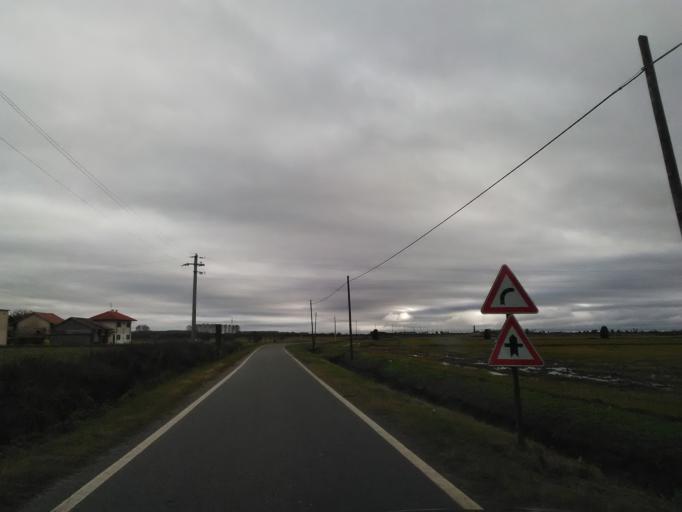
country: IT
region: Piedmont
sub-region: Provincia di Vercelli
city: Carisio
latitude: 45.4047
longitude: 8.2154
